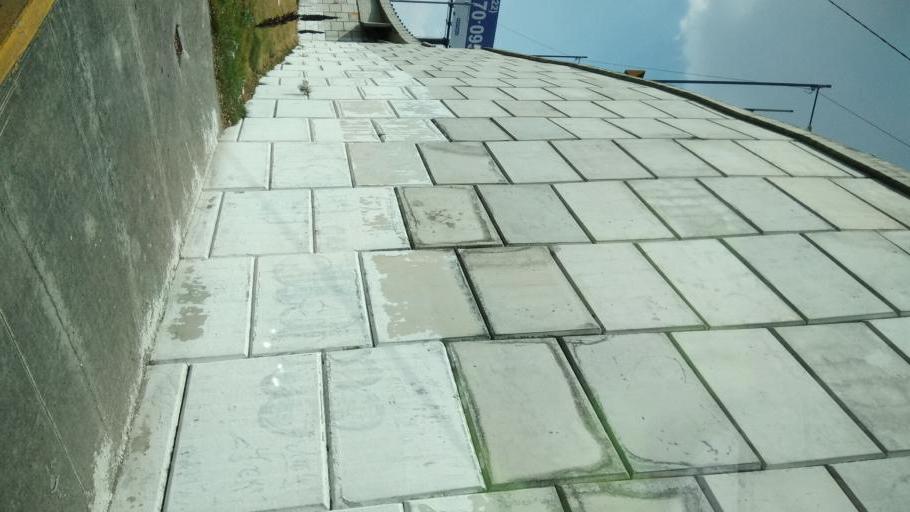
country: MX
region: Mexico
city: Santa Maria Totoltepec
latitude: 19.2870
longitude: -99.5763
